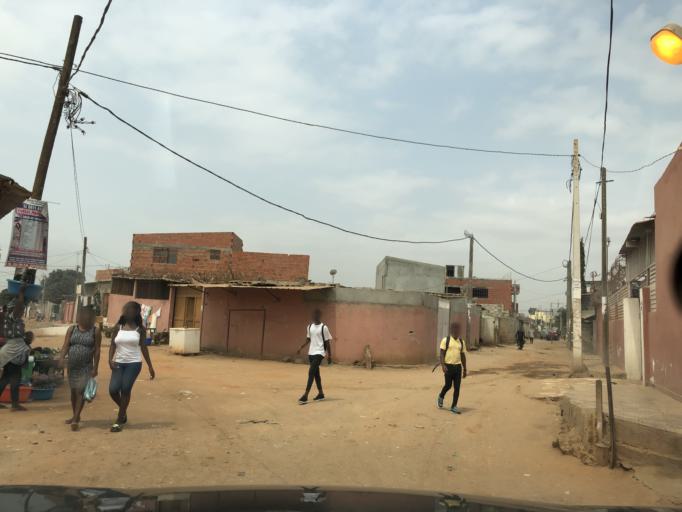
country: AO
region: Luanda
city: Luanda
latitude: -8.9118
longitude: 13.1725
